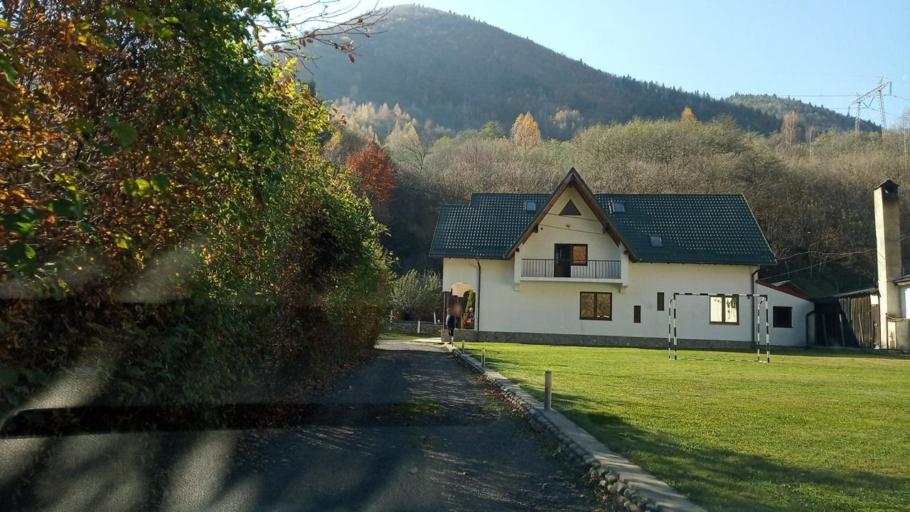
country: RO
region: Sibiu
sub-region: Comuna Boita
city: Boita
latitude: 45.5697
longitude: 24.2341
